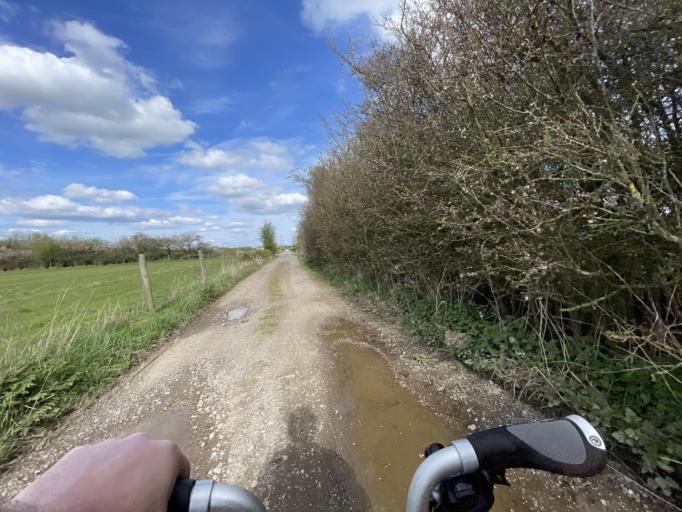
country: GB
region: England
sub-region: Warwickshire
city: Rugby
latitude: 52.3755
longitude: -1.1922
